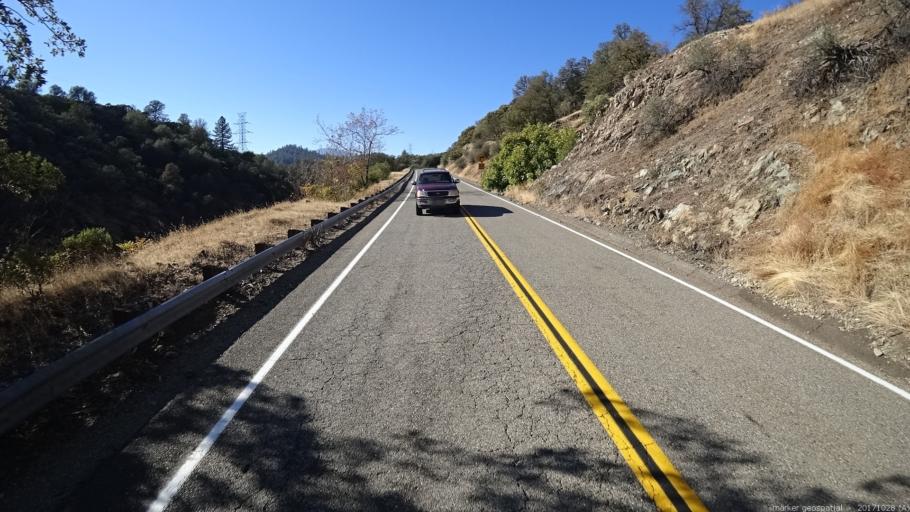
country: US
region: California
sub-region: Shasta County
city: Shasta
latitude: 40.6108
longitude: -122.4520
